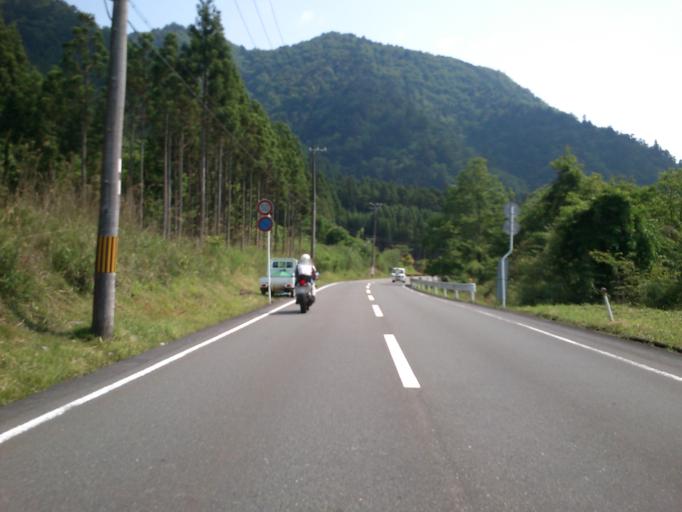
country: JP
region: Kyoto
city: Kameoka
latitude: 35.2611
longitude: 135.5718
